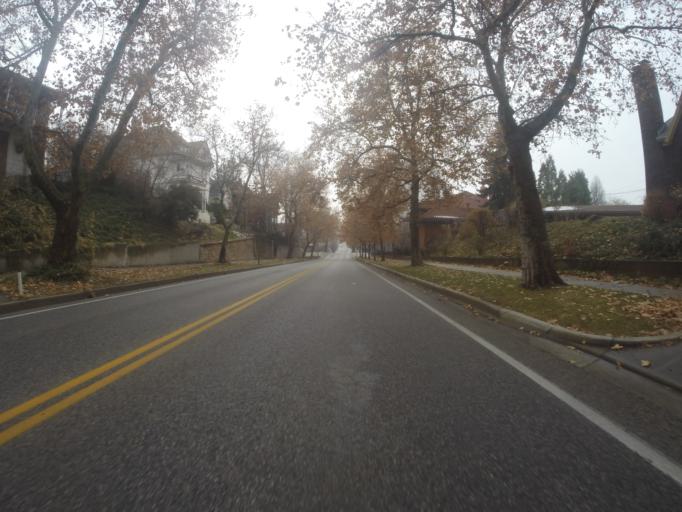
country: US
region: Utah
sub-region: Salt Lake County
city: Salt Lake City
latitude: 40.7746
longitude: -111.8883
